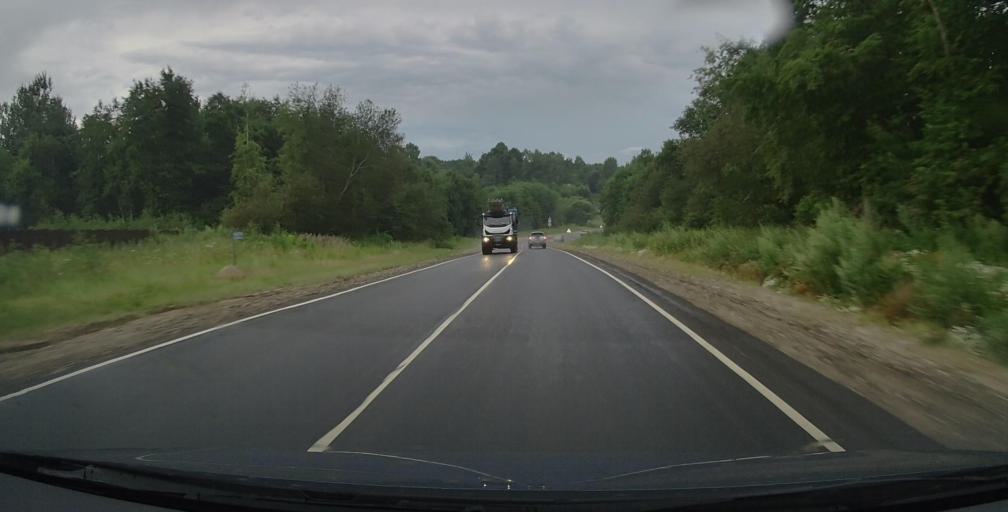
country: RU
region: Jaroslavl
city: Uglich
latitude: 57.5590
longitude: 38.2785
